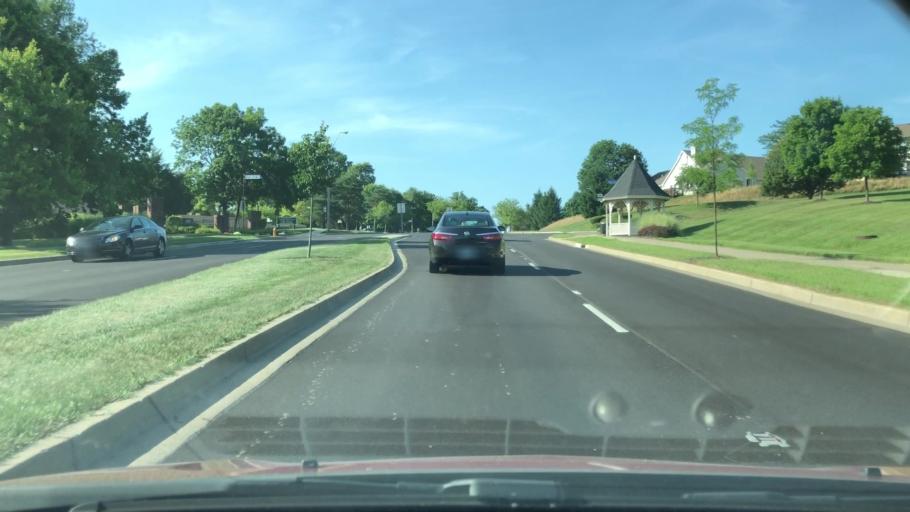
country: US
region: Ohio
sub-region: Montgomery County
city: Centerville
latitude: 39.6441
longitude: -84.1381
